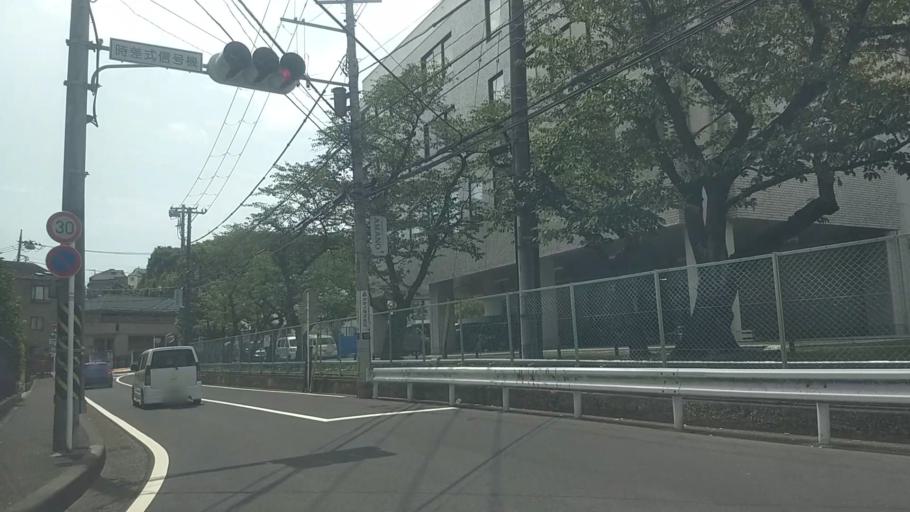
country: JP
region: Kanagawa
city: Yokohama
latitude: 35.5131
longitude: 139.6299
